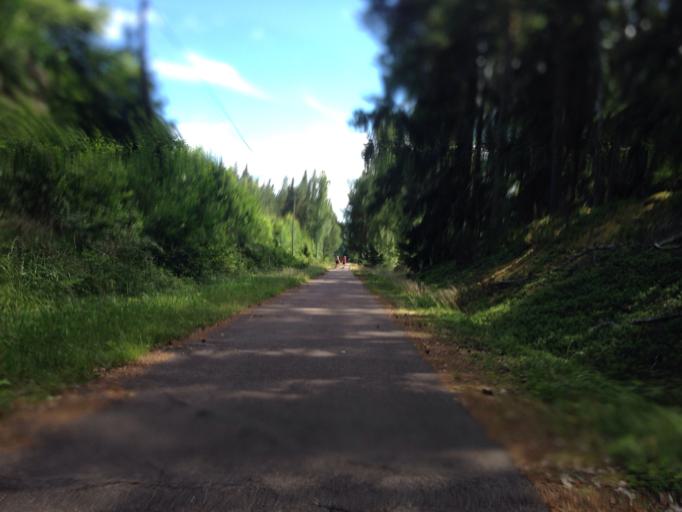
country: SE
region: Dalarna
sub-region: Ludvika Kommun
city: Grangesberg
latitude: 60.2279
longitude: 15.0329
